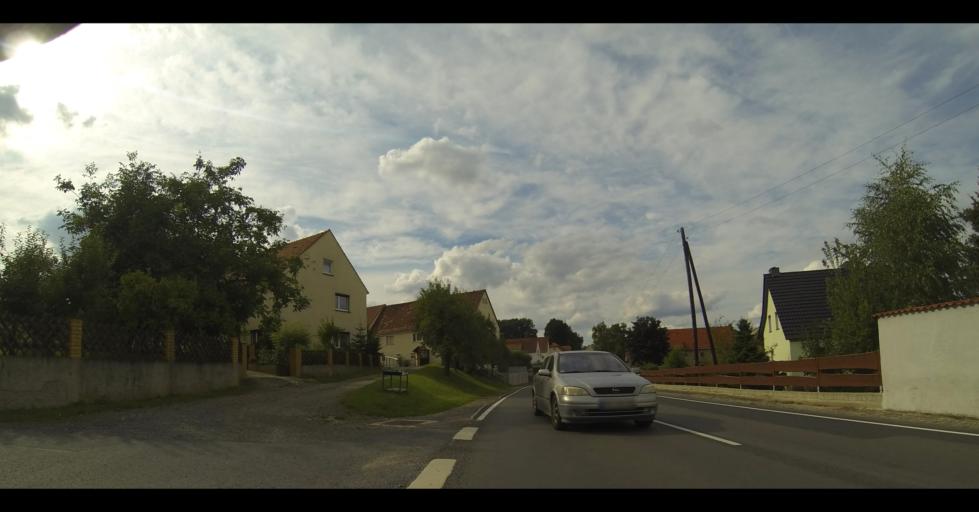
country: DE
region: Saxony
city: Radeburg
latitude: 51.2261
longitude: 13.7041
